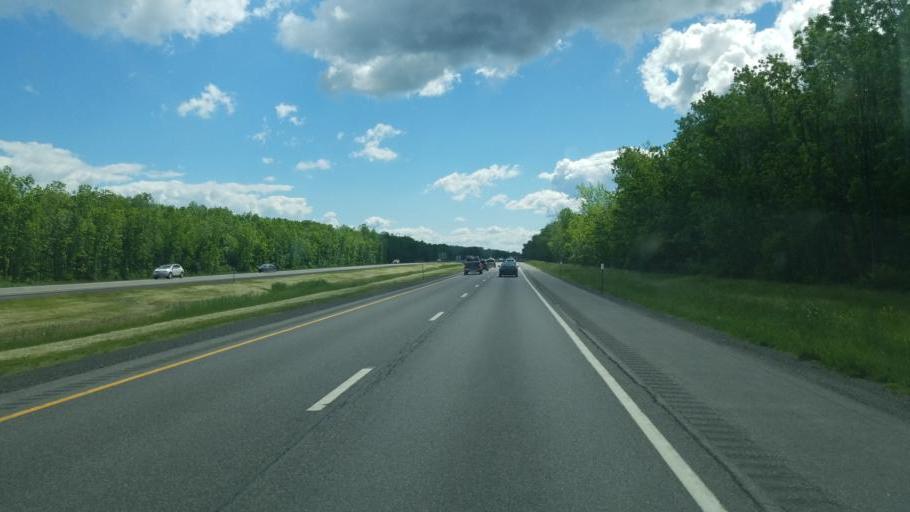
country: US
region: New York
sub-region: Madison County
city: Canastota
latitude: 43.0938
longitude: -75.8162
